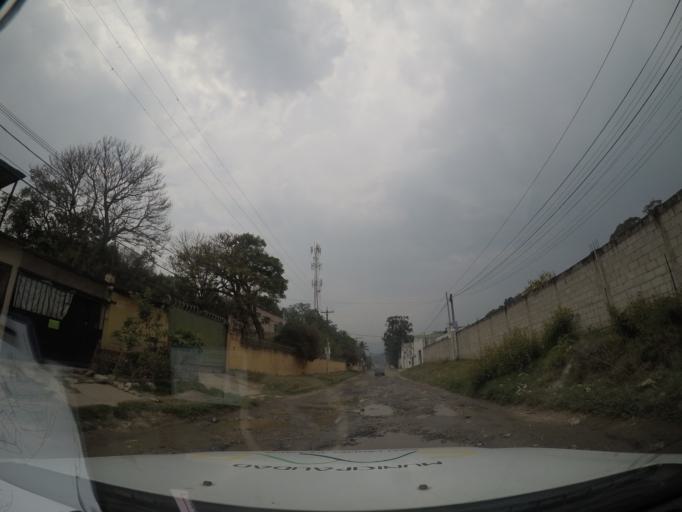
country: GT
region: Guatemala
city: Petapa
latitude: 14.5082
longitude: -90.5531
